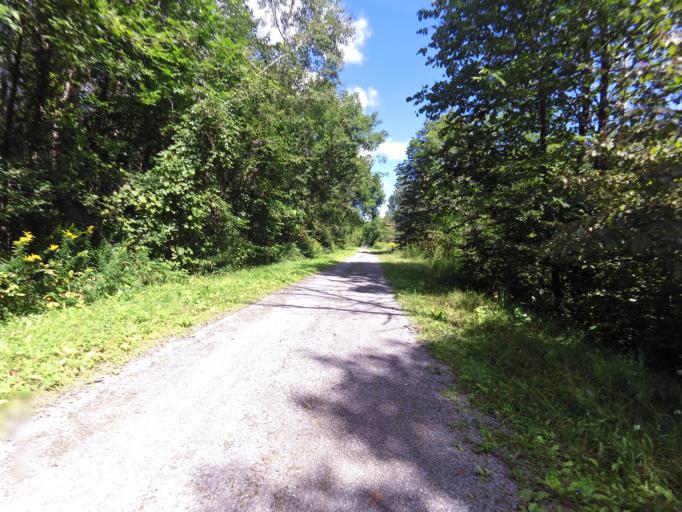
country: CA
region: Ontario
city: Ottawa
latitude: 45.2690
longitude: -75.6239
